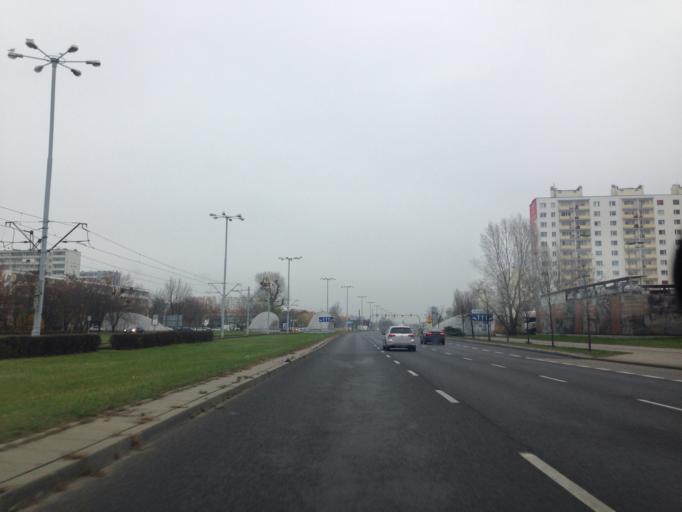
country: PL
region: Kujawsko-Pomorskie
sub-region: Torun
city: Torun
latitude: 53.0248
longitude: 18.6700
